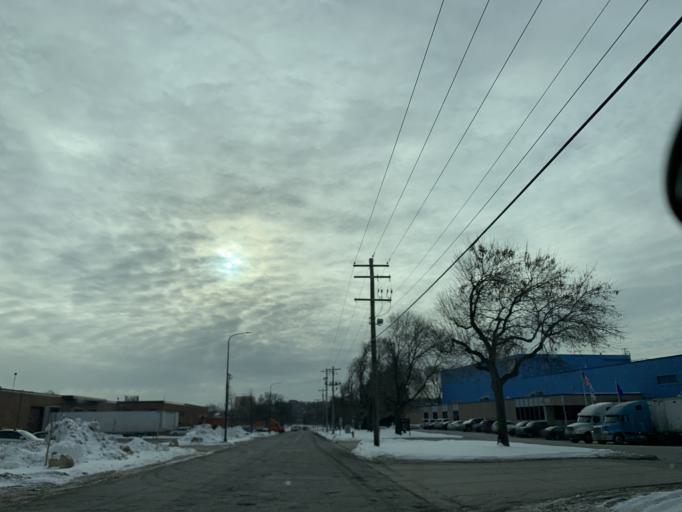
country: US
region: Minnesota
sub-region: Ramsey County
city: Saint Paul
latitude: 44.9413
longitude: -93.0816
